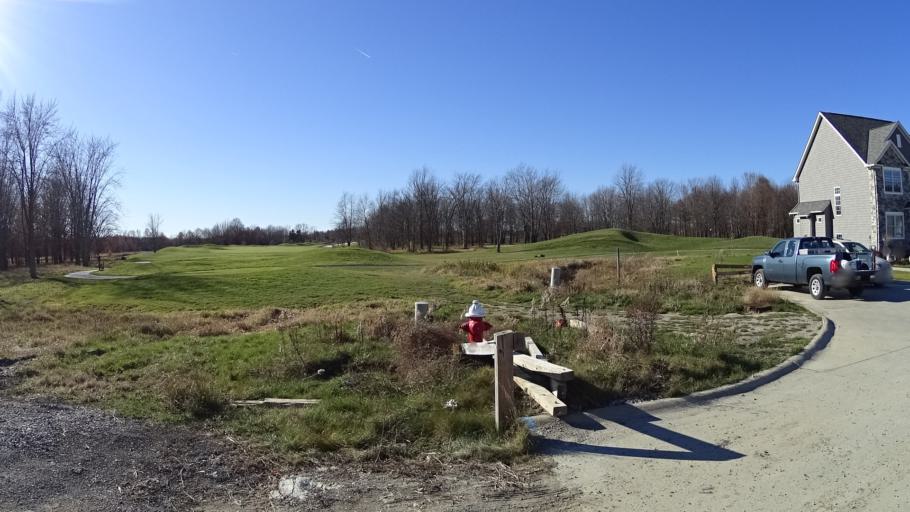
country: US
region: Ohio
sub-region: Lorain County
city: North Ridgeville
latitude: 41.4247
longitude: -81.9837
